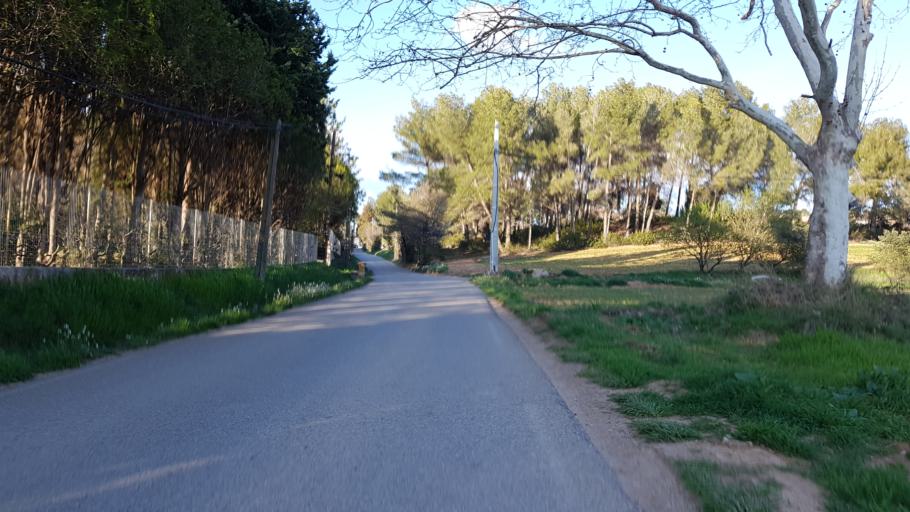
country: FR
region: Provence-Alpes-Cote d'Azur
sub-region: Departement des Bouches-du-Rhone
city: Bouc-Bel-Air
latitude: 43.4920
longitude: 5.3923
